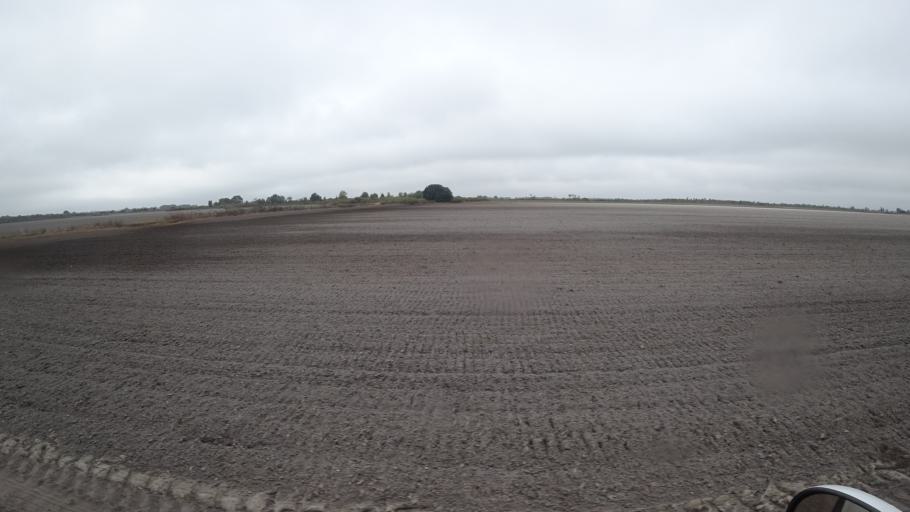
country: US
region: Florida
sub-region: Sarasota County
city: Warm Mineral Springs
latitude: 27.2853
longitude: -82.1754
